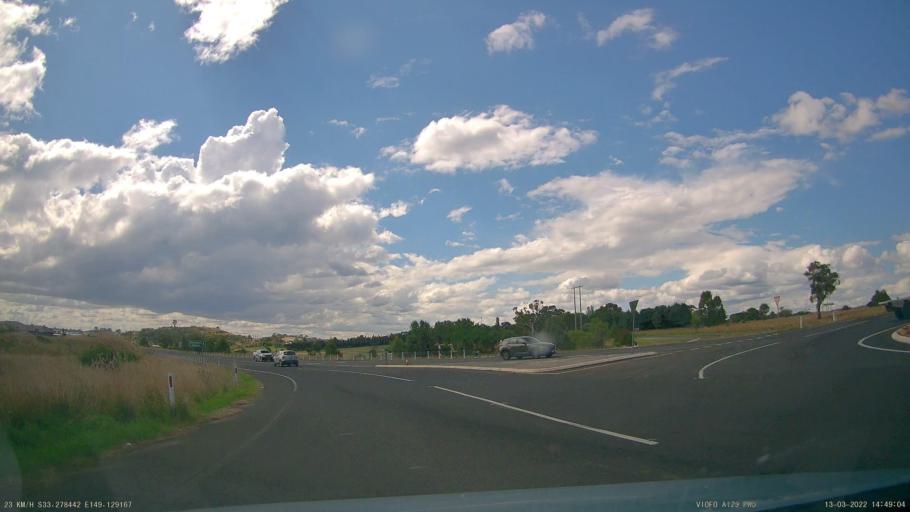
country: AU
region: New South Wales
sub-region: Orange Municipality
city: Orange
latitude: -33.2785
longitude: 149.1293
